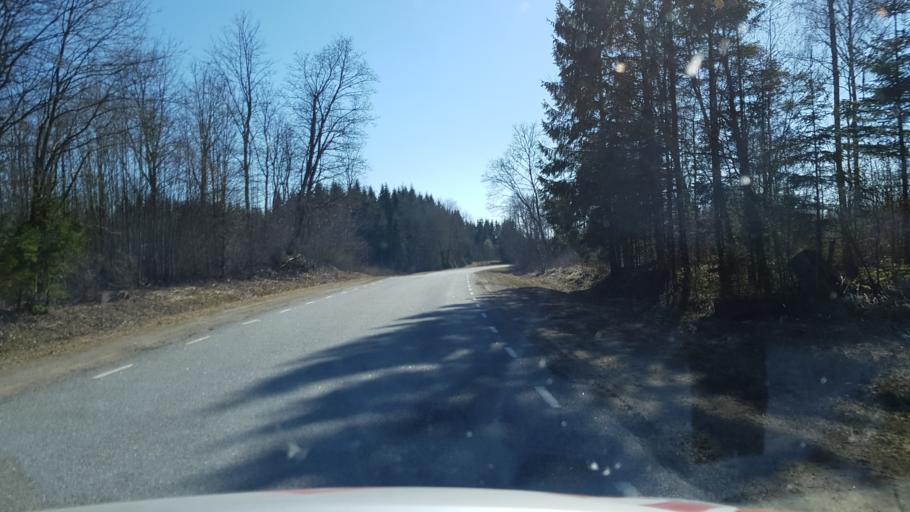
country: EE
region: Laeaene-Virumaa
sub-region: Tamsalu vald
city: Tamsalu
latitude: 59.0563
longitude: 26.1010
